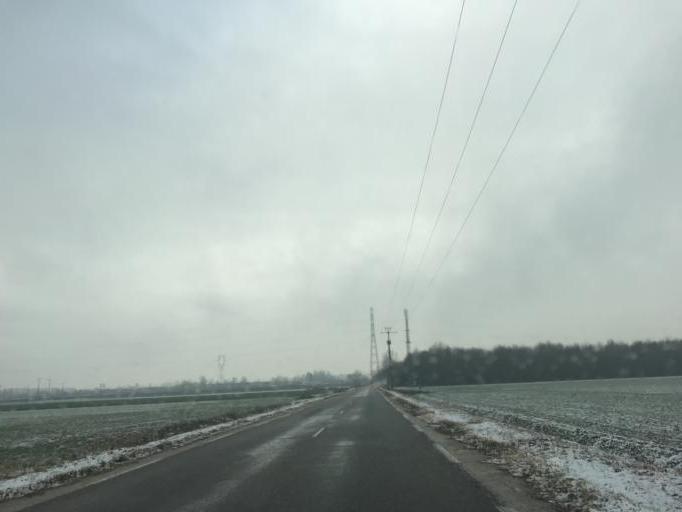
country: FR
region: Rhone-Alpes
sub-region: Departement de l'Ain
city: Tramoyes
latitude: 45.8539
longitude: 4.9589
